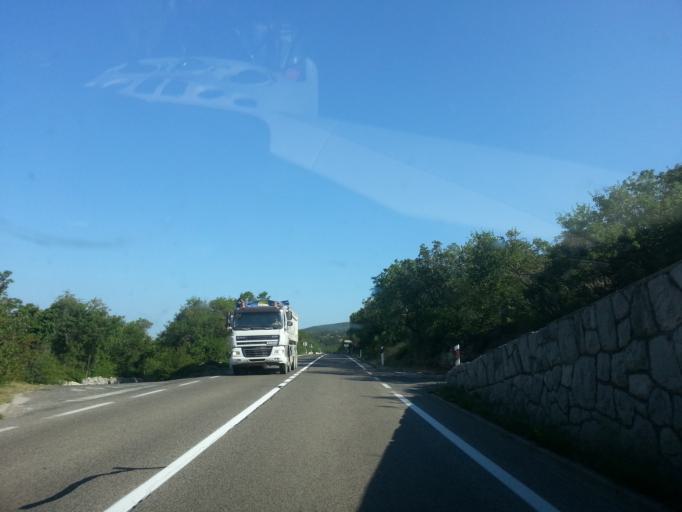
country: HR
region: Primorsko-Goranska
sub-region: Grad Crikvenica
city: Jadranovo
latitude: 45.2255
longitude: 14.6344
